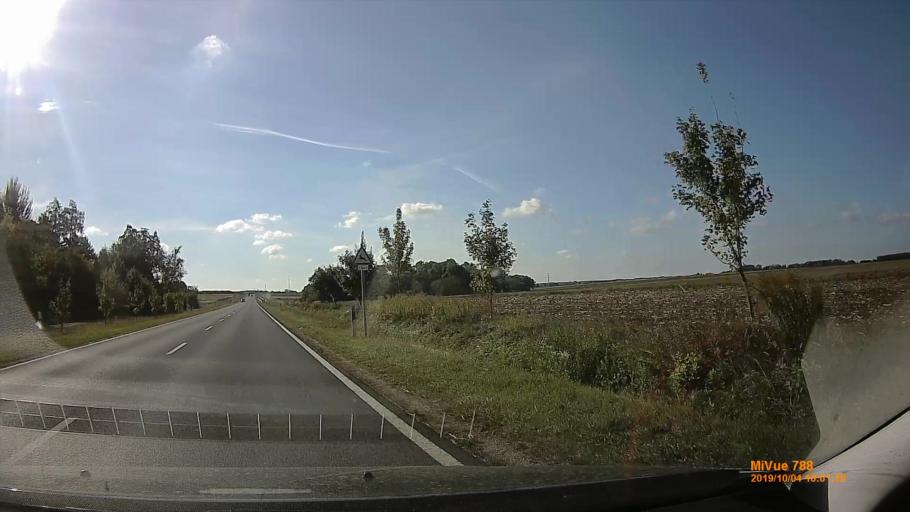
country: HU
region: Somogy
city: Kaposvar
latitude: 46.4087
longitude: 17.7720
